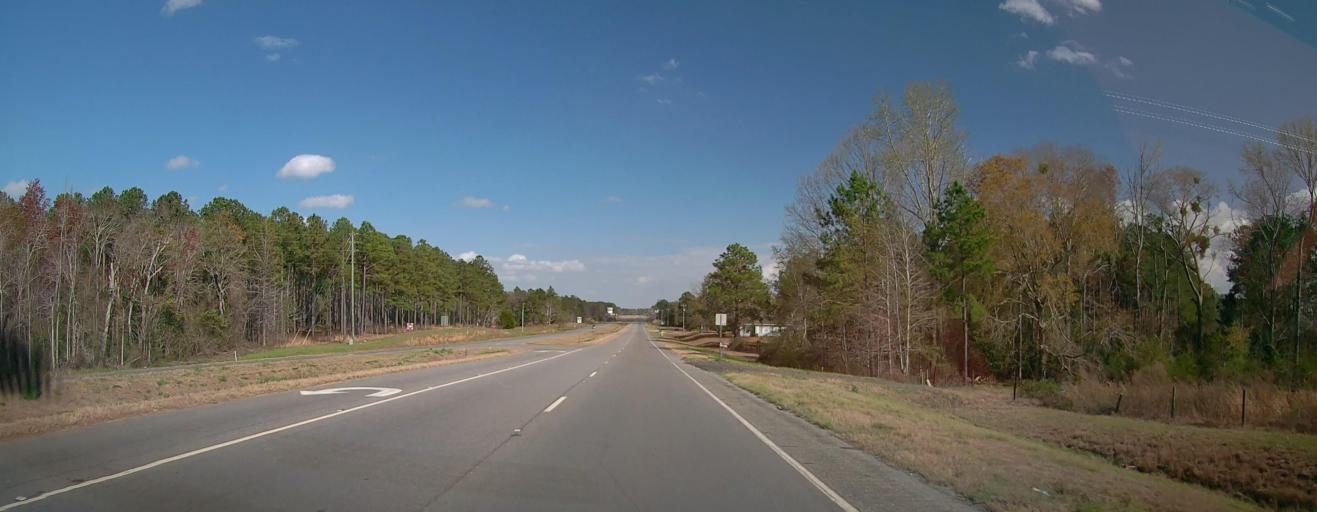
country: US
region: Georgia
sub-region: Dodge County
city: Eastman
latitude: 32.2027
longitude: -83.2792
